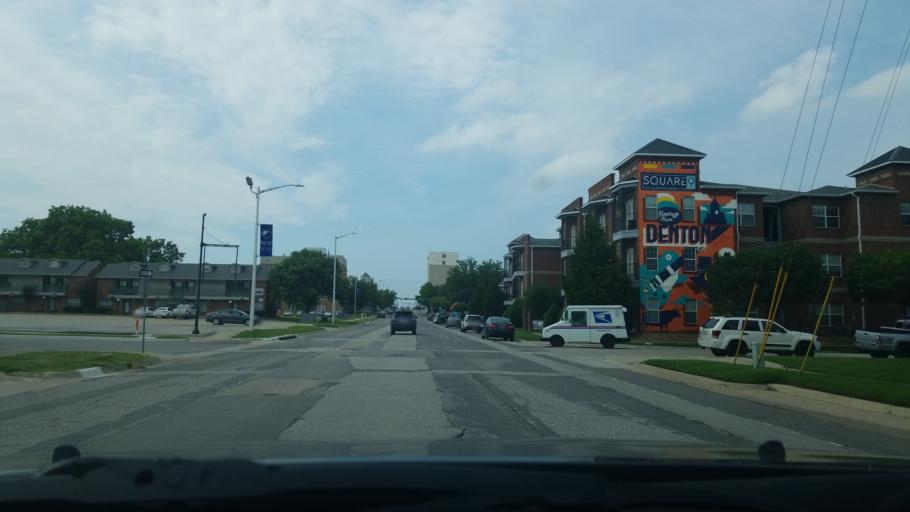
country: US
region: Texas
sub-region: Denton County
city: Denton
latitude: 33.2104
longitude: -97.1325
